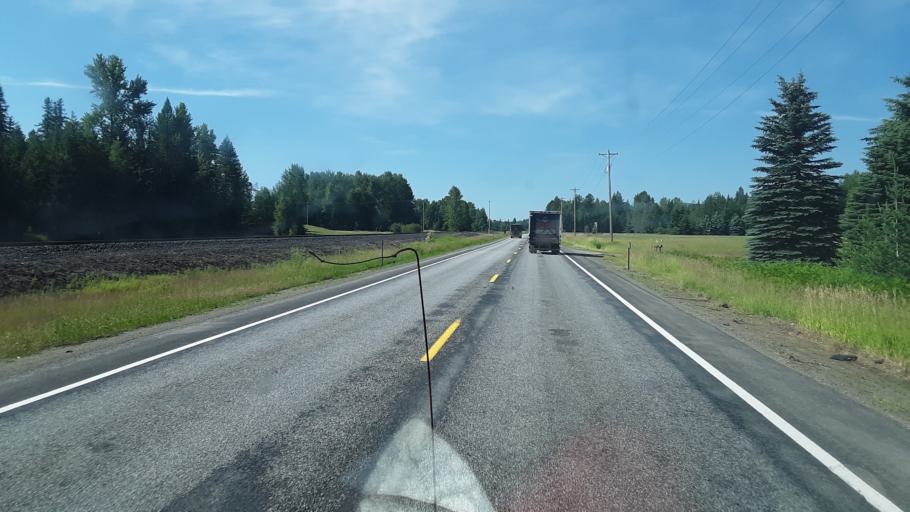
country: US
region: Idaho
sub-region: Bonner County
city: Ponderay
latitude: 48.4627
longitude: -116.4722
